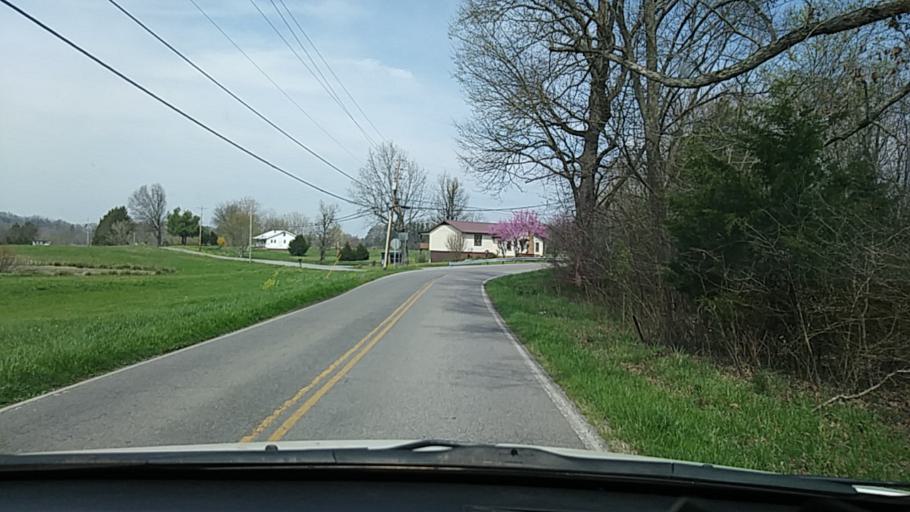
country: US
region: Tennessee
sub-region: Greene County
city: Tusculum
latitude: 36.0992
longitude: -82.7444
